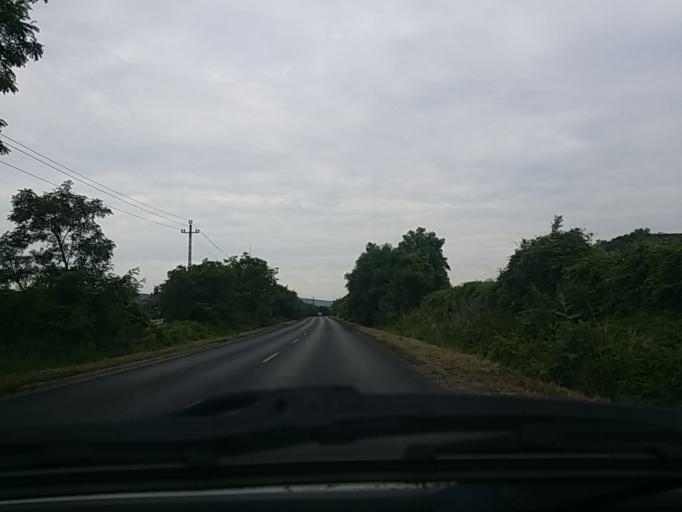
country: HU
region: Pest
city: Csobanka
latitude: 47.6541
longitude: 18.9824
